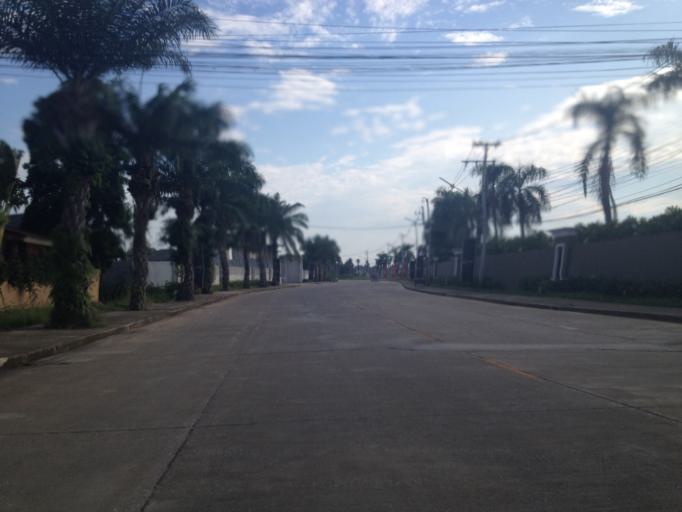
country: TH
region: Chiang Mai
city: Hang Dong
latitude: 18.7217
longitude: 98.9153
